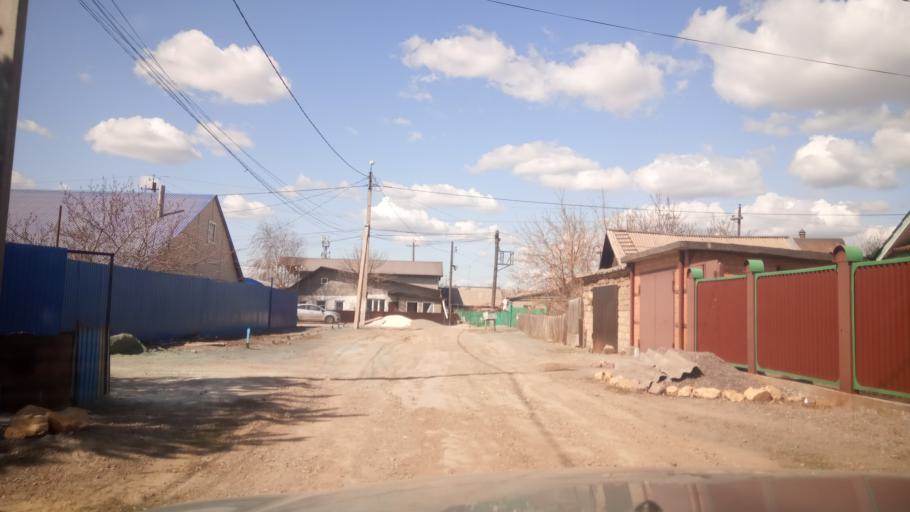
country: RU
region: Orenburg
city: Novotroitsk
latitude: 51.2114
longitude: 58.3152
